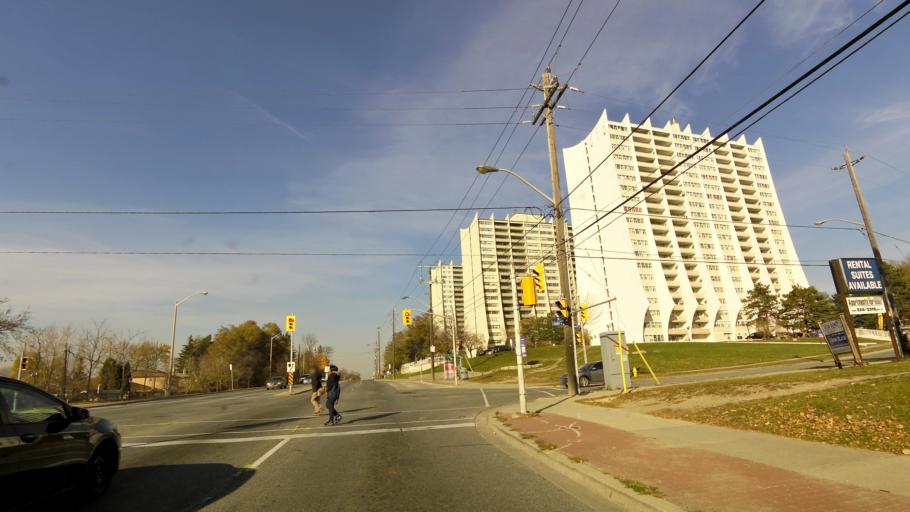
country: CA
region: Ontario
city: Concord
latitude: 43.7292
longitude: -79.5105
